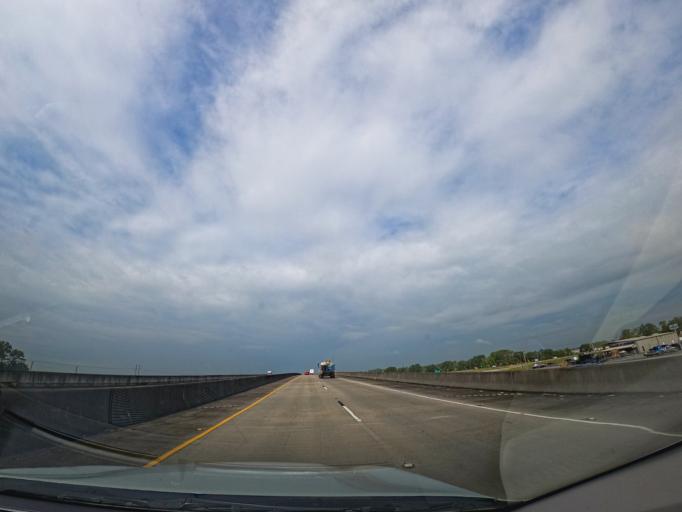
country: US
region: Louisiana
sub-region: Iberia Parish
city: New Iberia
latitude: 29.9411
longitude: -91.7692
